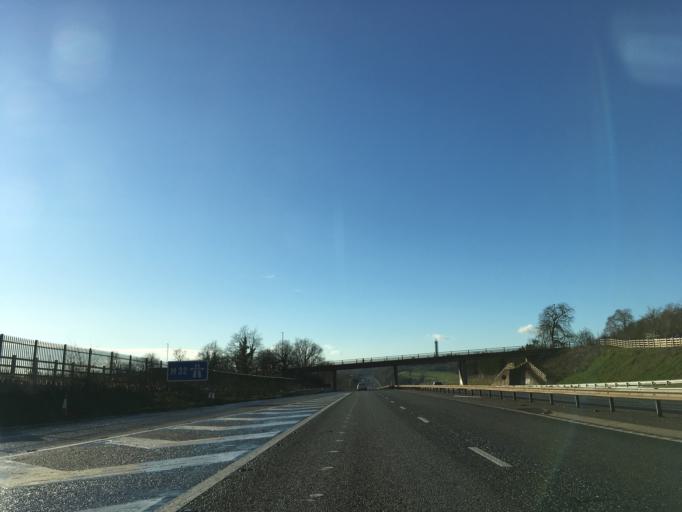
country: GB
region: England
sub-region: South Gloucestershire
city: Stoke Gifford
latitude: 51.4934
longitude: -2.5397
